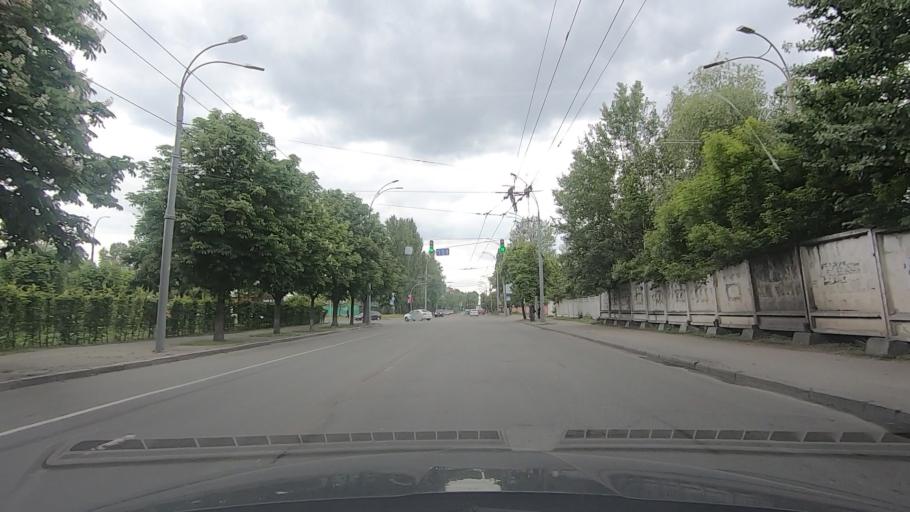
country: MD
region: Drochia
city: Drochia
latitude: 48.0819
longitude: 27.8576
